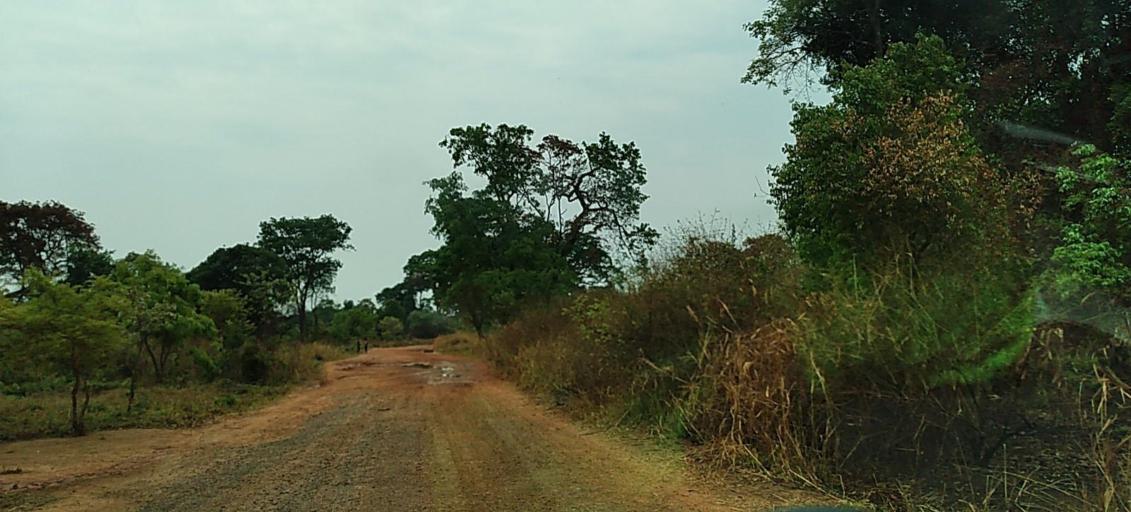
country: ZM
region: North-Western
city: Solwezi
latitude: -12.3425
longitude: 26.5269
